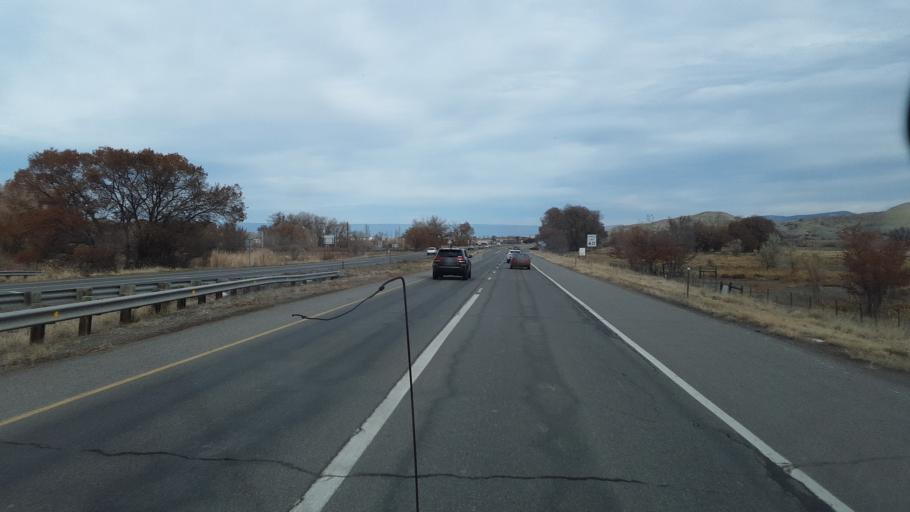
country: US
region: Colorado
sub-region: Montrose County
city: Montrose
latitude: 38.4365
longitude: -107.8664
